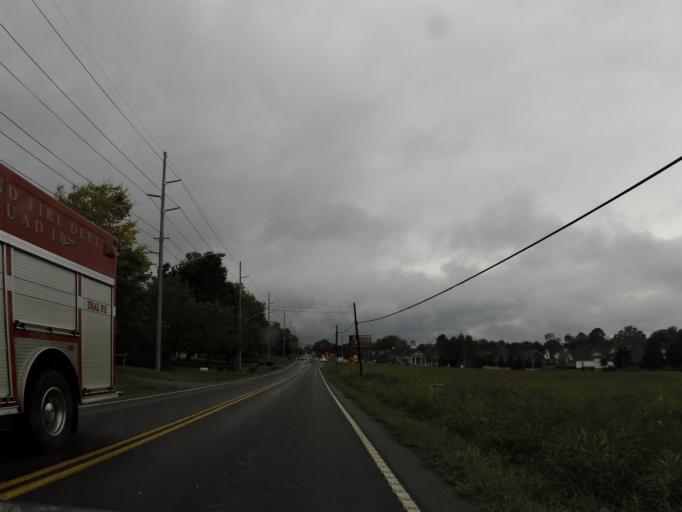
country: US
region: Tennessee
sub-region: Bradley County
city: Hopewell
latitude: 35.2096
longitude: -84.8853
